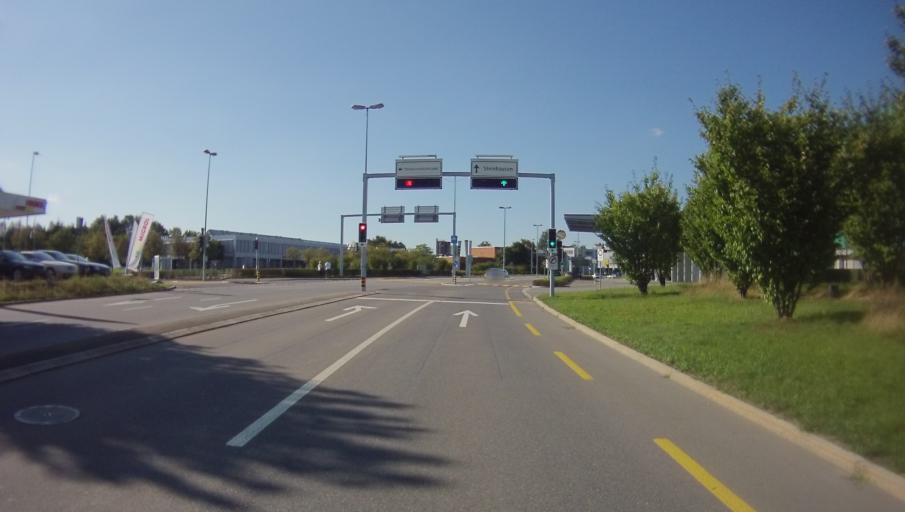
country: CH
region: Zug
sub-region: Zug
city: Steinhausen
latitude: 47.1907
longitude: 8.4775
